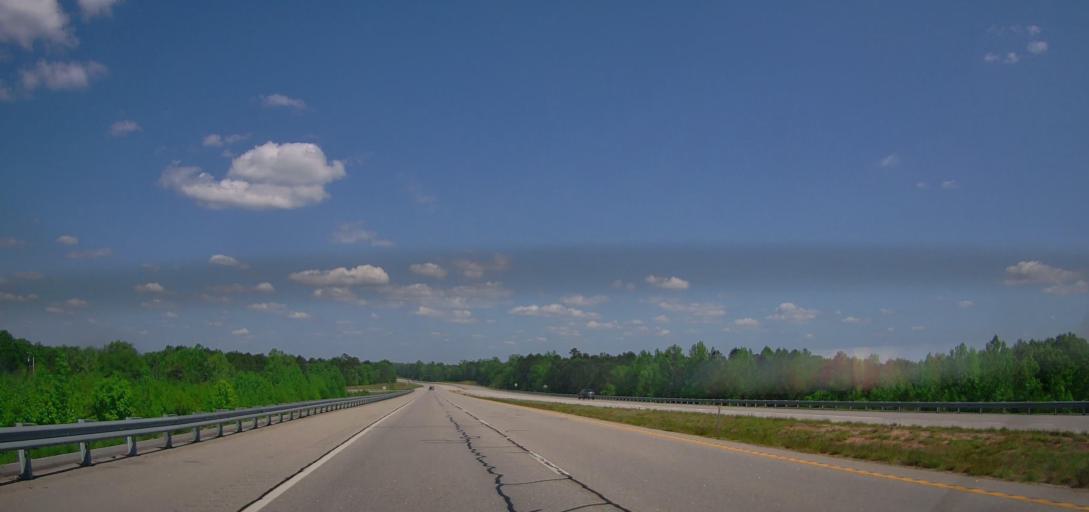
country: US
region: Georgia
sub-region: Putnam County
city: Eatonton
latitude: 33.2742
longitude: -83.3646
